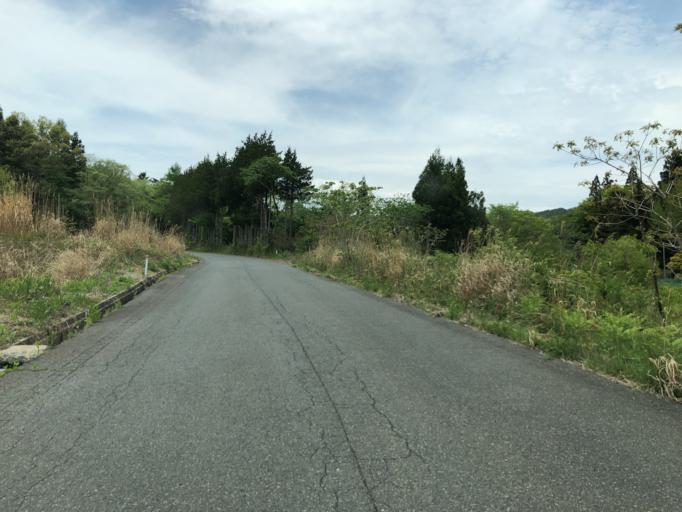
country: JP
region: Miyagi
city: Marumori
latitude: 37.7246
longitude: 140.7904
